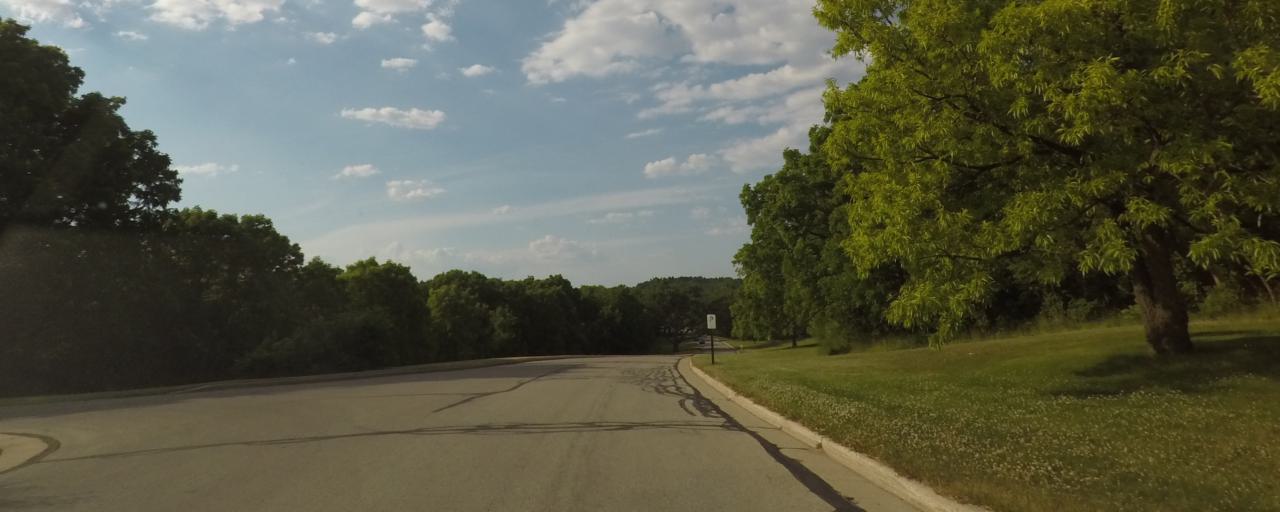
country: US
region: Wisconsin
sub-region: Milwaukee County
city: Hales Corners
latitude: 42.9266
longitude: -88.0295
